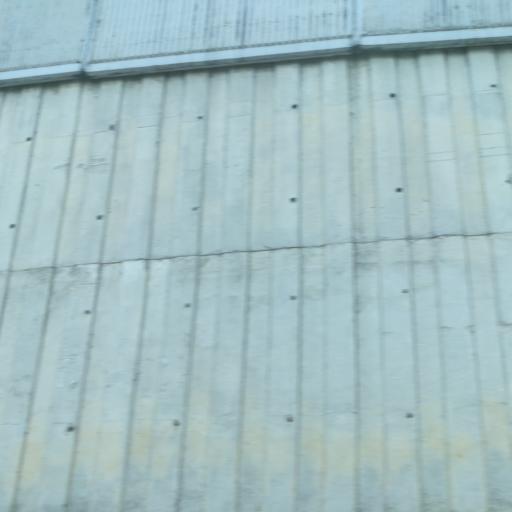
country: NG
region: Rivers
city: Port Harcourt
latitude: 4.8098
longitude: 7.0624
